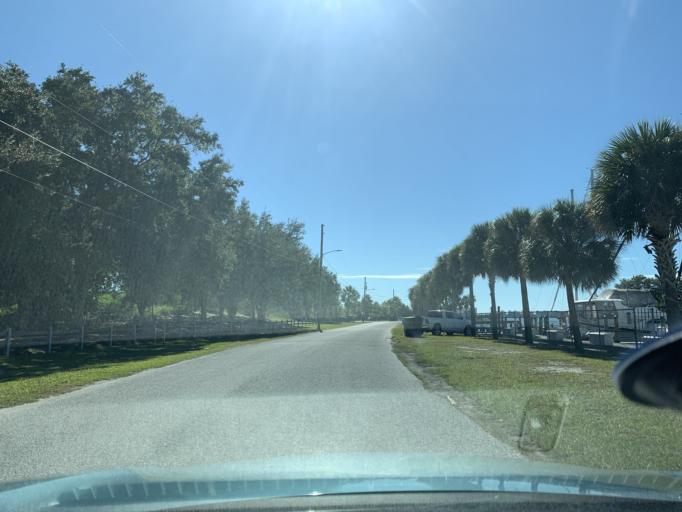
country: US
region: Florida
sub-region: Pinellas County
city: Gulfport
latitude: 27.7400
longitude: -82.6946
